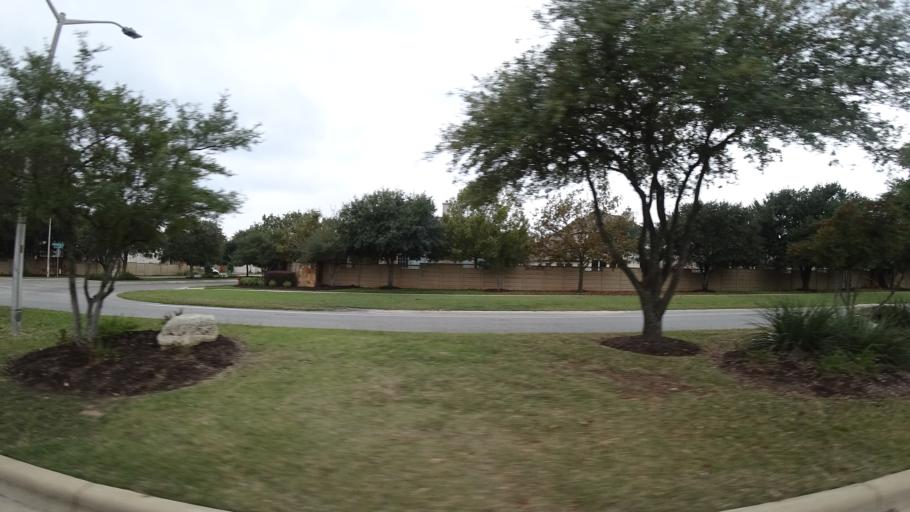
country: US
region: Texas
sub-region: Williamson County
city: Cedar Park
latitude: 30.4759
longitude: -97.8521
